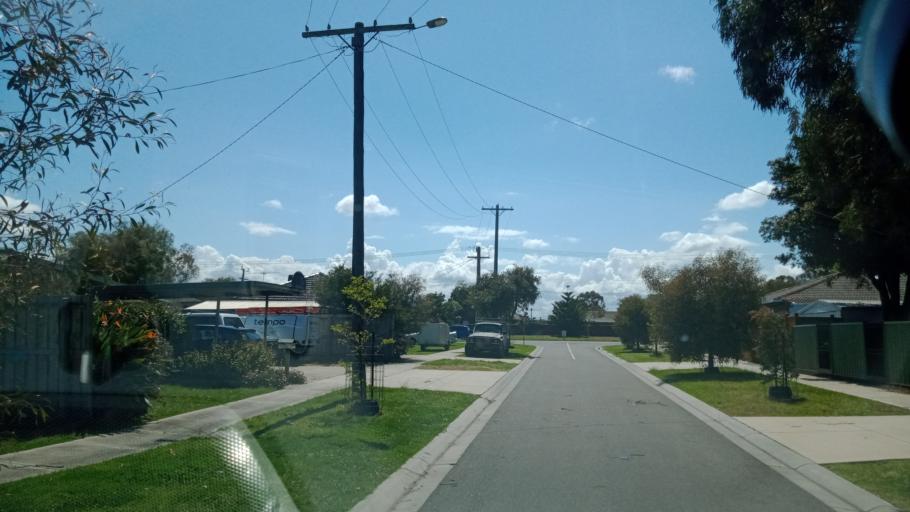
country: AU
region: Victoria
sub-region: Casey
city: Cranbourne West
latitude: -38.0972
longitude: 145.2698
